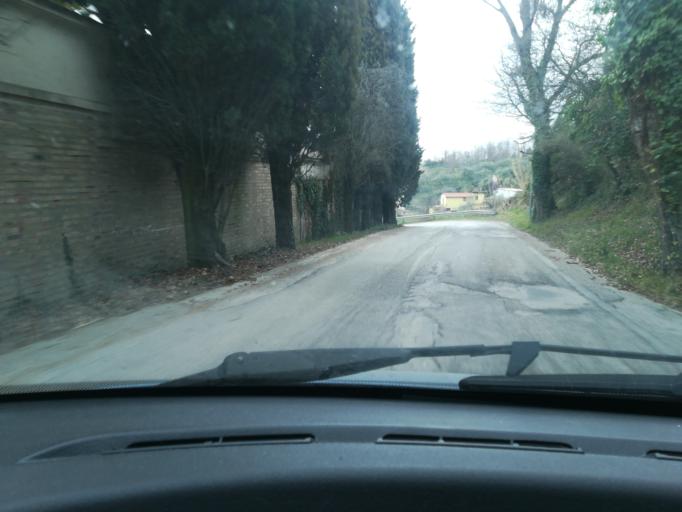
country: IT
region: The Marches
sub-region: Provincia di Macerata
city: Macerata
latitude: 43.2933
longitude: 13.4641
